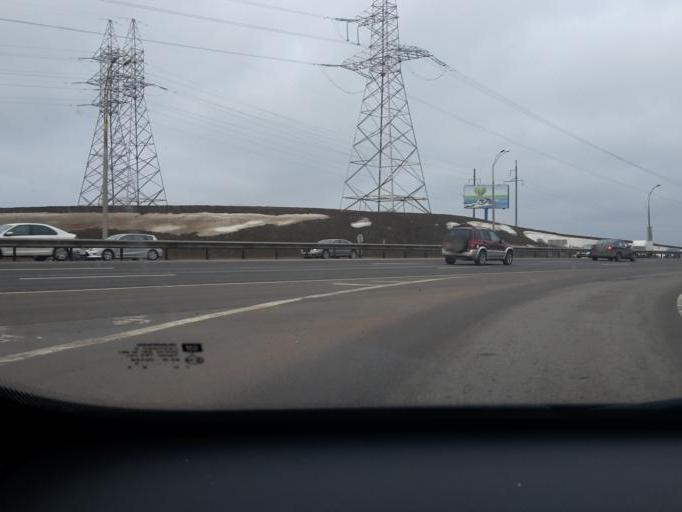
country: BY
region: Minsk
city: Malinovka
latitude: 53.8808
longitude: 27.4178
